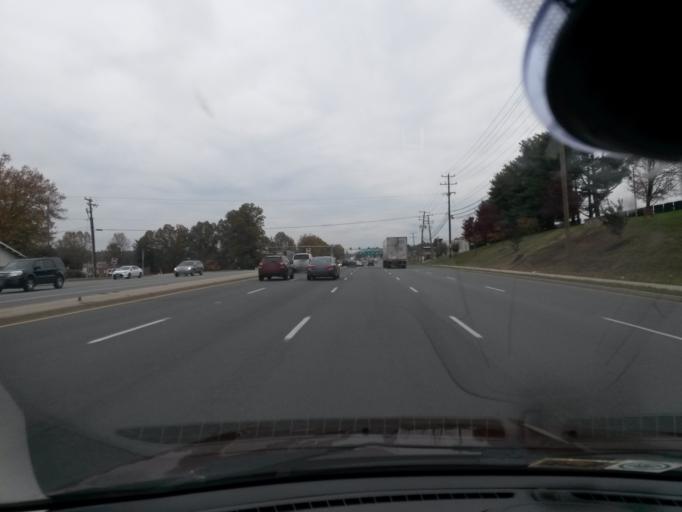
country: US
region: Virginia
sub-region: City of Charlottesville
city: Charlottesville
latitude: 38.0690
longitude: -78.4855
